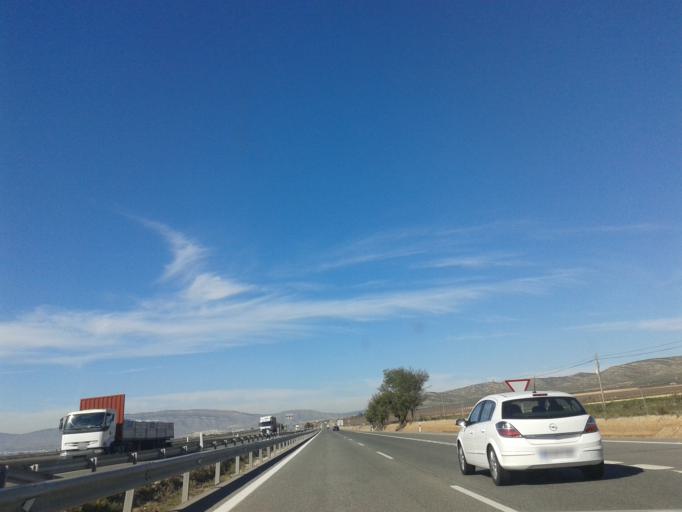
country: ES
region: Valencia
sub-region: Provincia de Alicante
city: Villena
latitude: 38.6730
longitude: -0.8889
